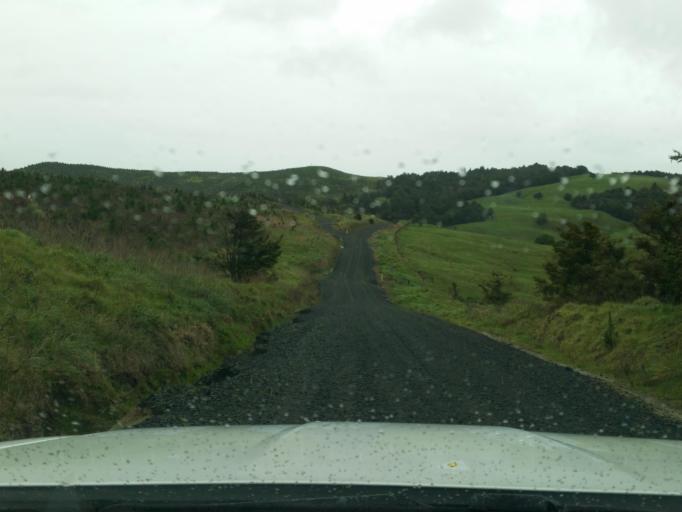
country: NZ
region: Northland
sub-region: Kaipara District
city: Dargaville
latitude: -35.8559
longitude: 173.8789
